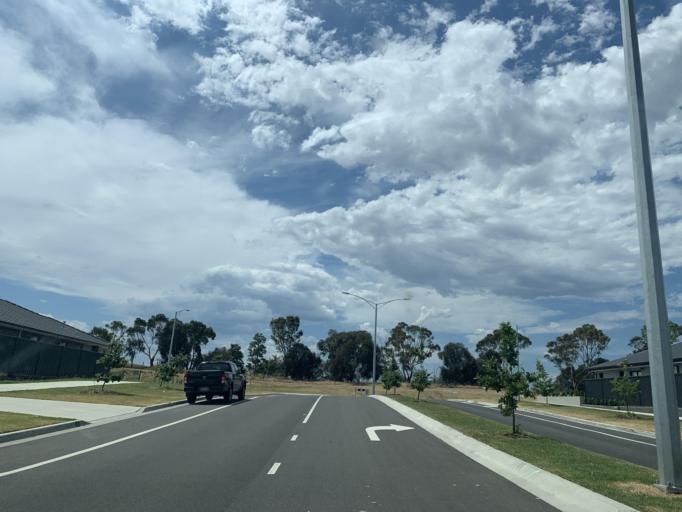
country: AU
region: Victoria
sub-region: Casey
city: Cranbourne South
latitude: -38.1237
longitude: 145.2410
